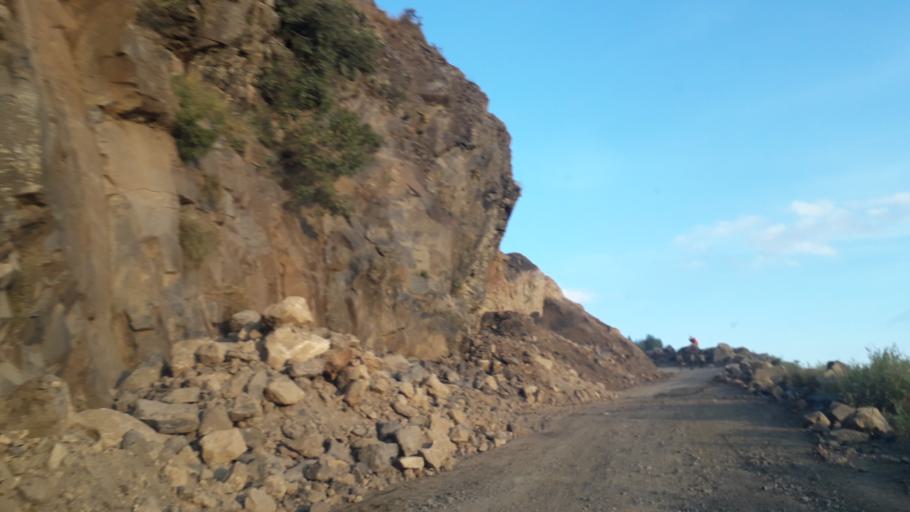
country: ET
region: Amhara
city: Lalibela
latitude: 11.5535
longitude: 39.2204
